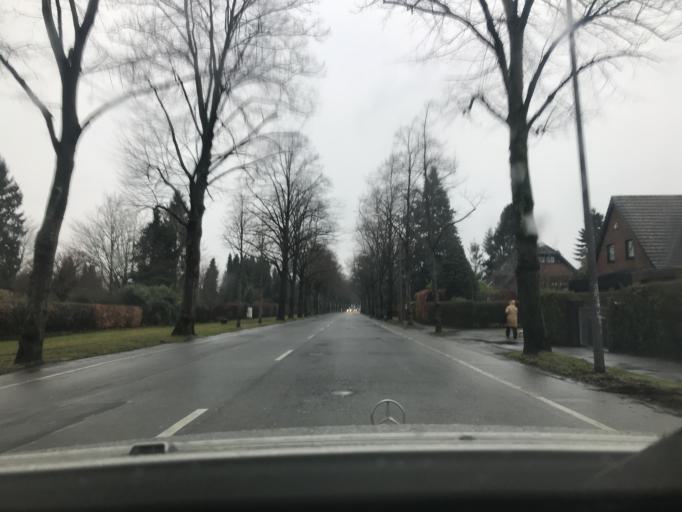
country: DE
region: North Rhine-Westphalia
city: Tonisvorst
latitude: 51.3147
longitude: 6.5338
